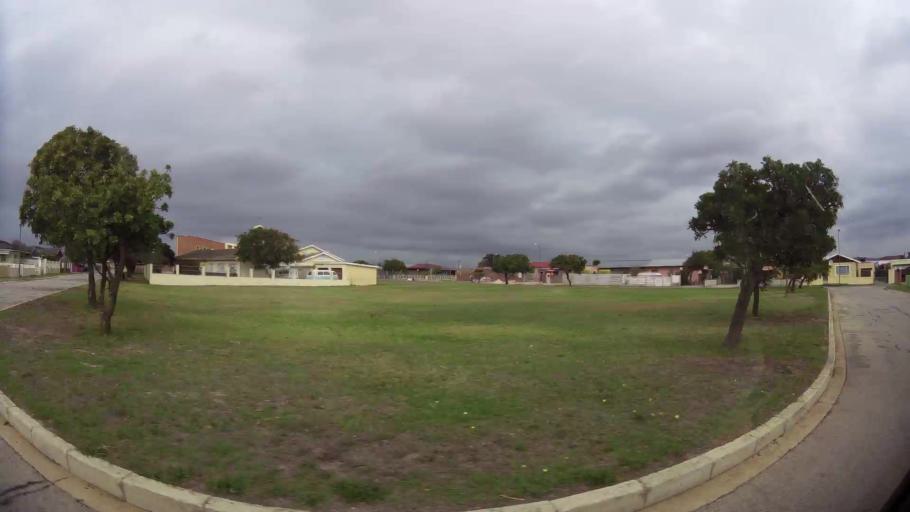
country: ZA
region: Eastern Cape
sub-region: Nelson Mandela Bay Metropolitan Municipality
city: Port Elizabeth
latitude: -33.8952
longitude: 25.5646
